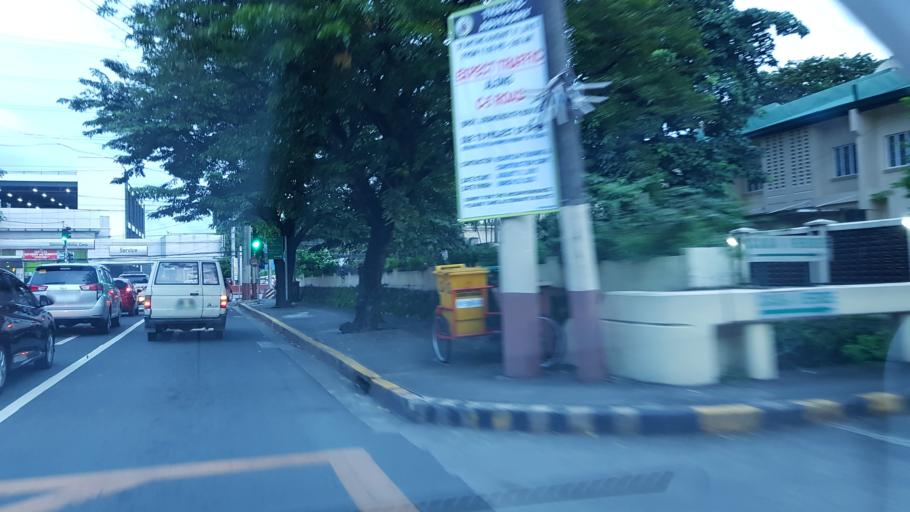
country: PH
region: Metro Manila
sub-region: Pasig
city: Pasig City
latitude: 14.5780
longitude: 121.0729
